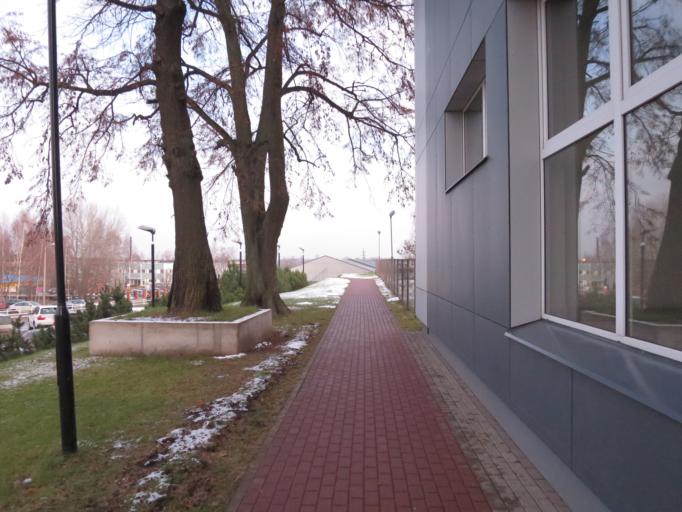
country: LV
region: Riga
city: Riga
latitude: 56.9152
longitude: 24.1132
